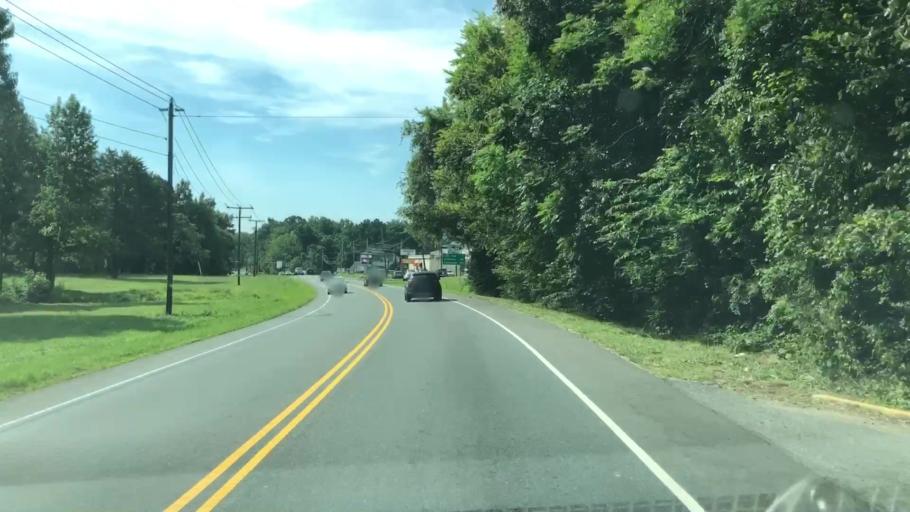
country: US
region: Virginia
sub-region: City of Fredericksburg
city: Fredericksburg
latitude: 38.2789
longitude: -77.4531
